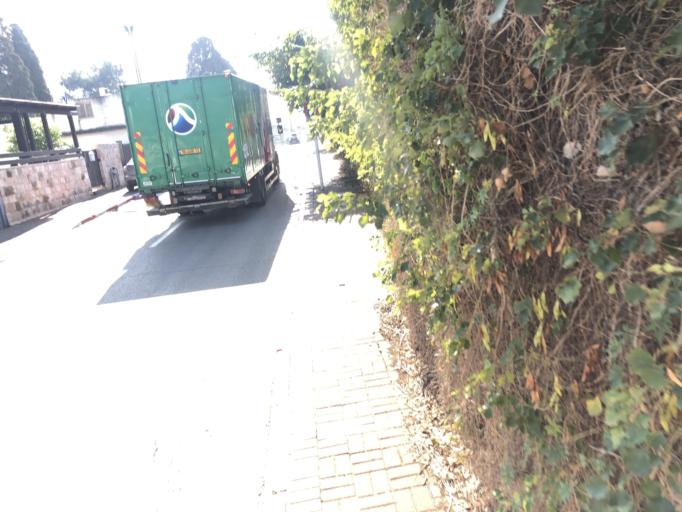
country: IL
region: Northern District
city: `Akko
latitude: 32.9380
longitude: 35.0919
